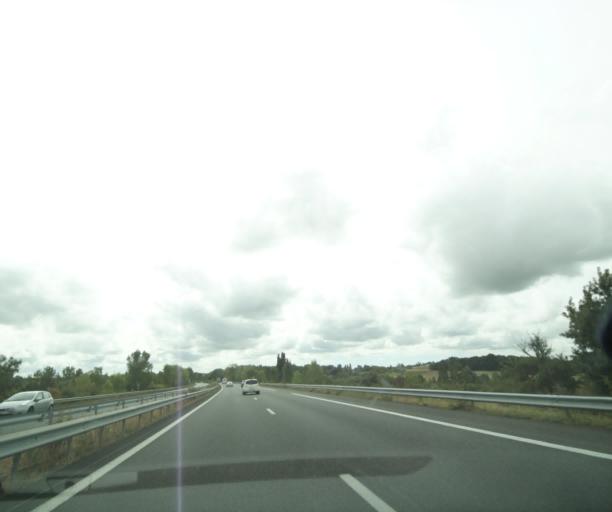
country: FR
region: Poitou-Charentes
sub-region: Departement de la Charente-Maritime
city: Mirambeau
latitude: 45.3846
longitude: -0.6031
